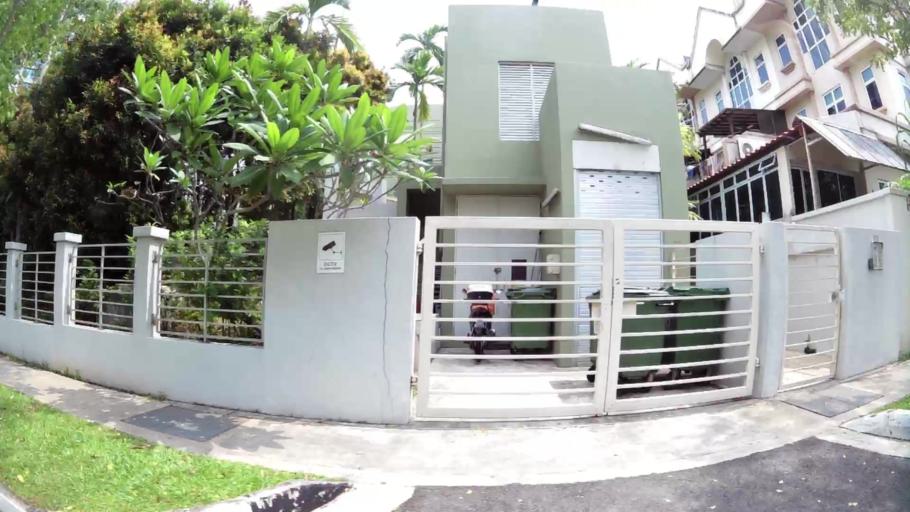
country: MY
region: Johor
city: Kampung Pasir Gudang Baru
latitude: 1.3726
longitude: 103.9407
